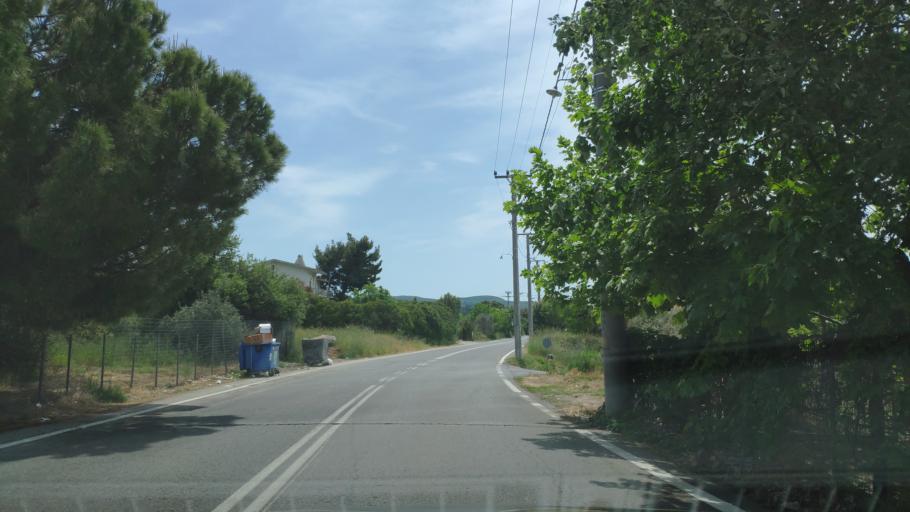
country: GR
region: Attica
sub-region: Nomarchia Anatolikis Attikis
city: Kapandriti
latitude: 38.2121
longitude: 23.8824
